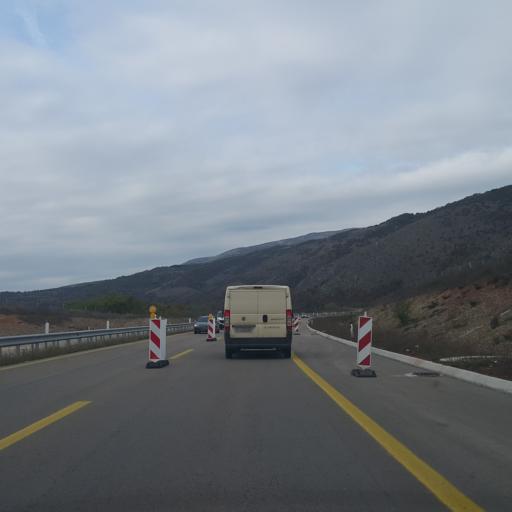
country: RS
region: Central Serbia
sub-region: Pirotski Okrug
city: Bela Palanka
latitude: 43.2276
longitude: 22.3831
